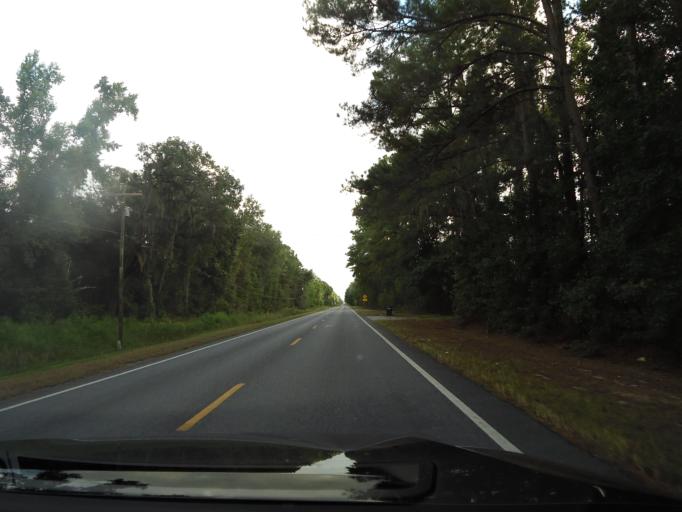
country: US
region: Georgia
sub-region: Liberty County
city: Midway
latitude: 31.6962
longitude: -81.4113
